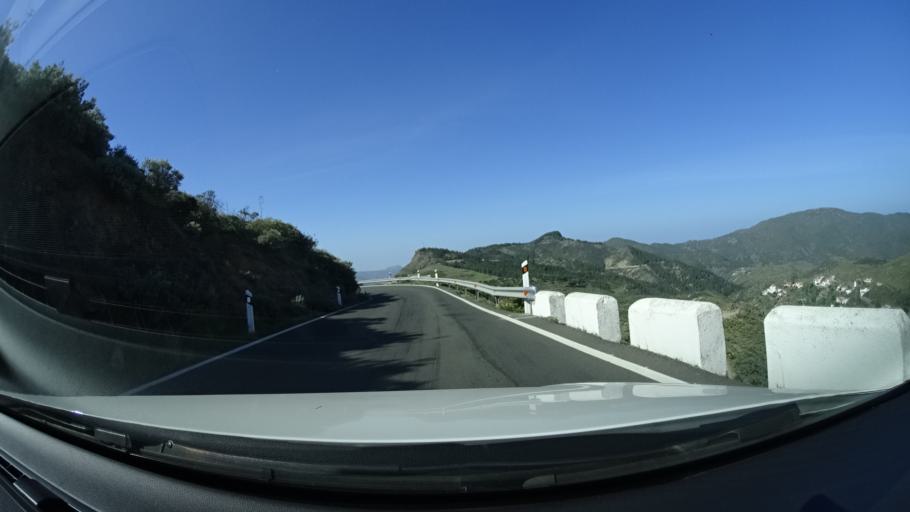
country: ES
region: Canary Islands
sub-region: Provincia de Las Palmas
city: Artenara
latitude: 28.0255
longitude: -15.6431
